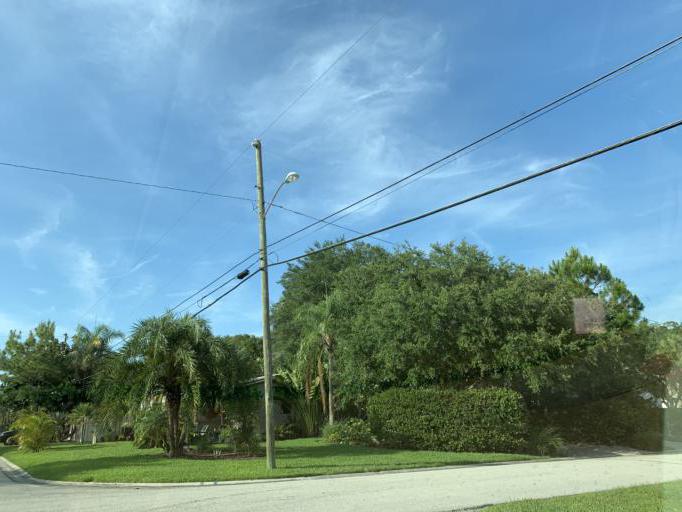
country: US
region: Florida
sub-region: Pinellas County
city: Lealman
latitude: 27.8039
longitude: -82.6289
